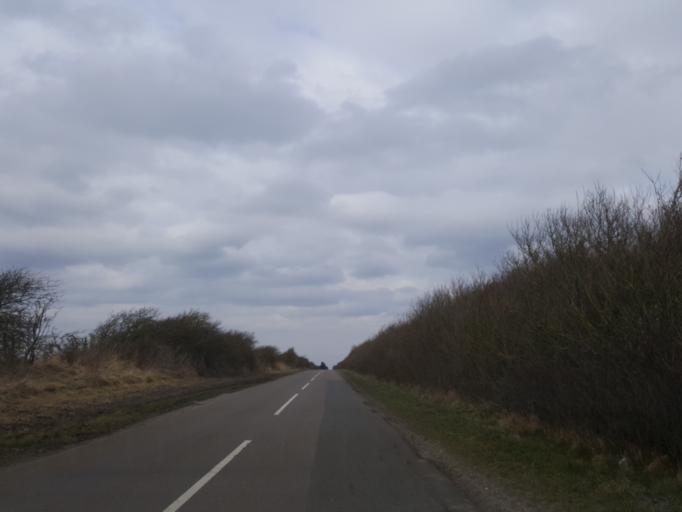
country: DK
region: Central Jutland
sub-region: Holstebro Kommune
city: Ulfborg
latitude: 56.3993
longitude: 8.2336
